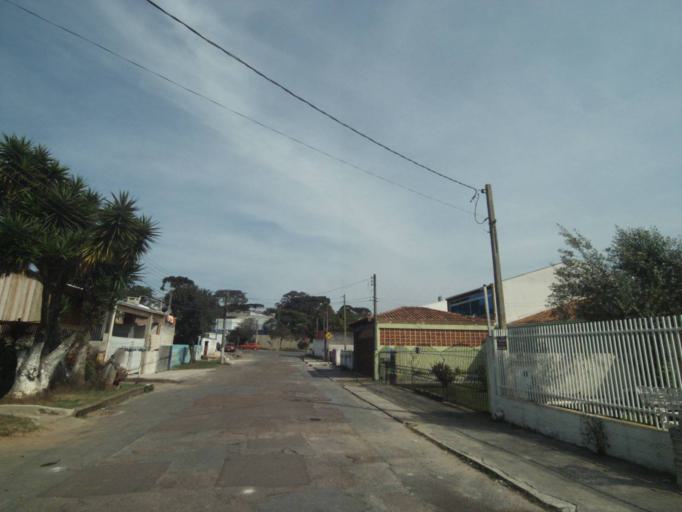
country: BR
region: Parana
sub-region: Curitiba
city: Curitiba
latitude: -25.4637
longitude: -49.3174
